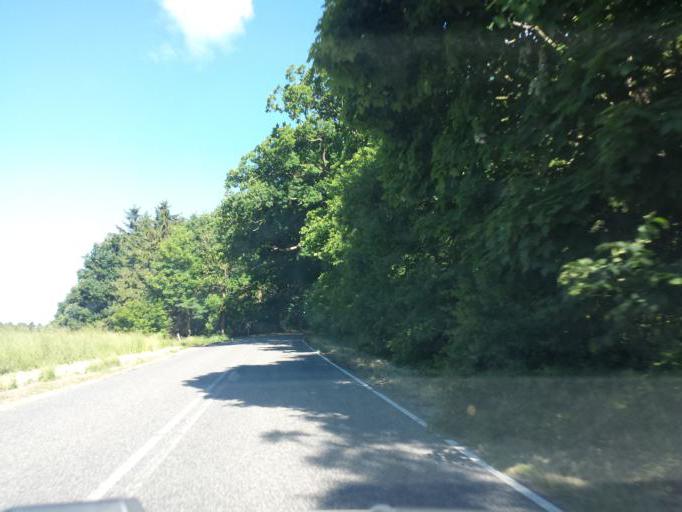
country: DK
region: Capital Region
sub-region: Egedal Kommune
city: Ganlose
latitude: 55.8056
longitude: 12.2631
